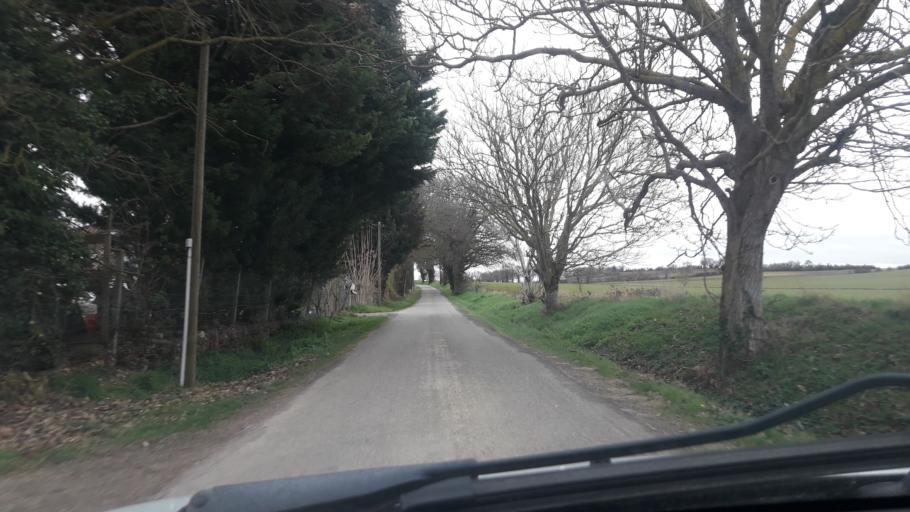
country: FR
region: Midi-Pyrenees
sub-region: Departement du Gers
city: Gimont
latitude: 43.6448
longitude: 0.9758
